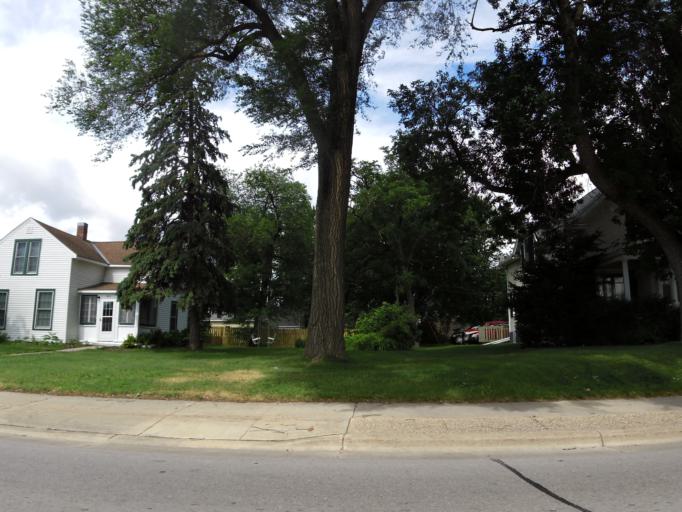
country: US
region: Minnesota
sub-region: Olmsted County
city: Stewartville
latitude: 43.8572
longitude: -92.4886
